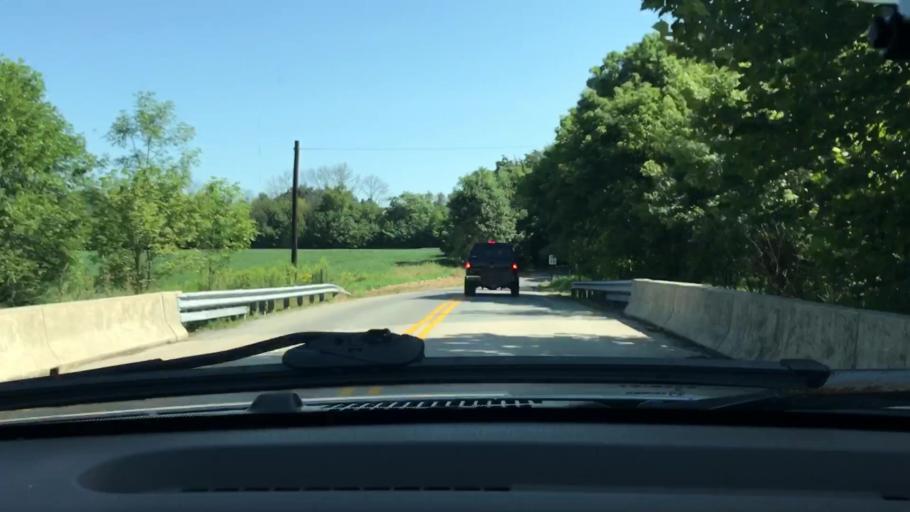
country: US
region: Pennsylvania
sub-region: Lancaster County
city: Elizabethtown
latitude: 40.1840
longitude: -76.6123
